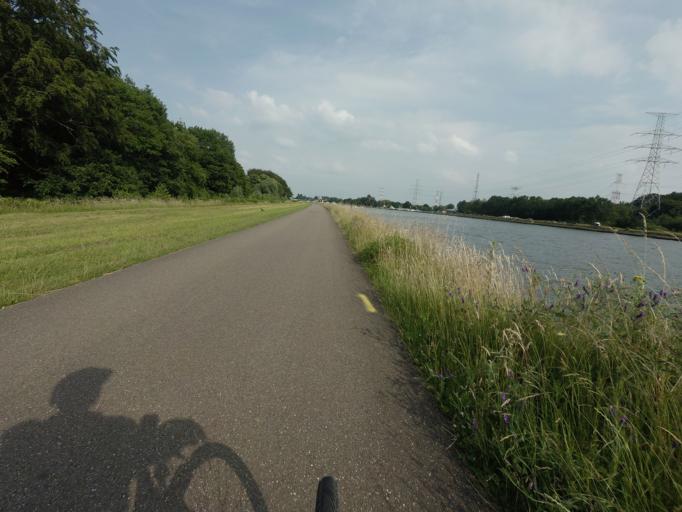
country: BE
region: Flanders
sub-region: Provincie Antwerpen
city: Zandhoven
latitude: 51.1996
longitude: 4.6247
